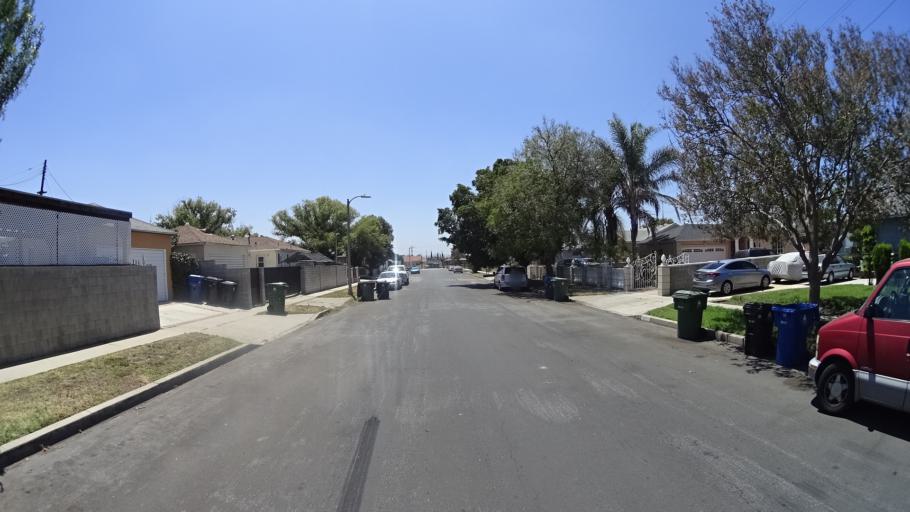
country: US
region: California
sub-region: Los Angeles County
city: San Fernando
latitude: 34.2358
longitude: -118.4297
